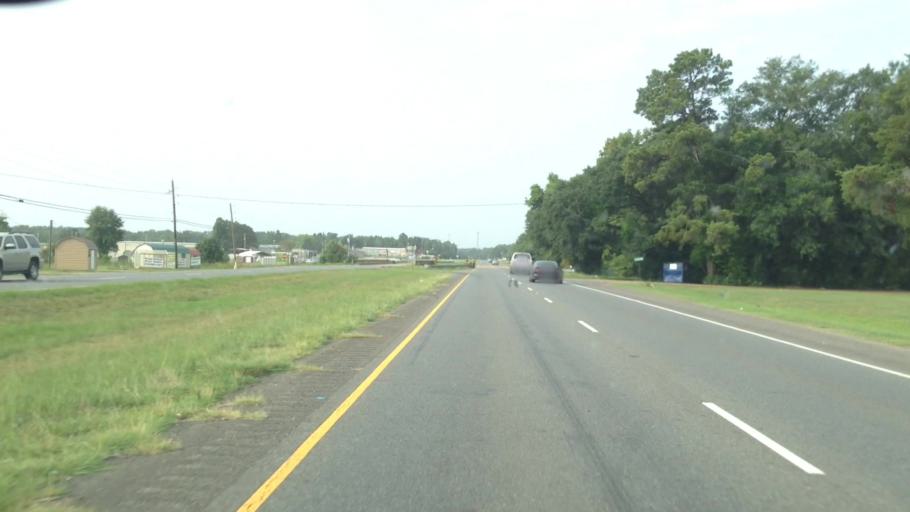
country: US
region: Louisiana
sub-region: De Soto Parish
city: Stonewall
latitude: 32.3703
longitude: -93.8238
